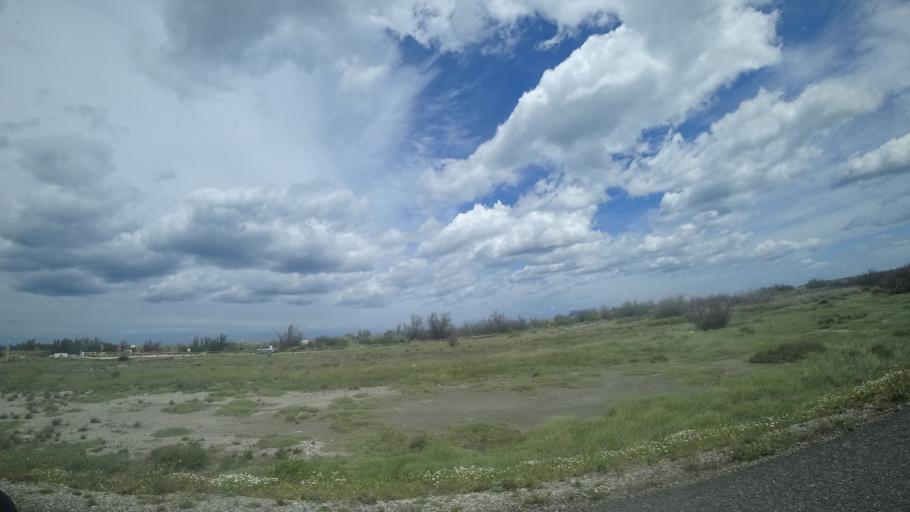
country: FR
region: Languedoc-Roussillon
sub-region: Departement de l'Aude
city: Leucate
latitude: 42.8895
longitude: 3.0485
